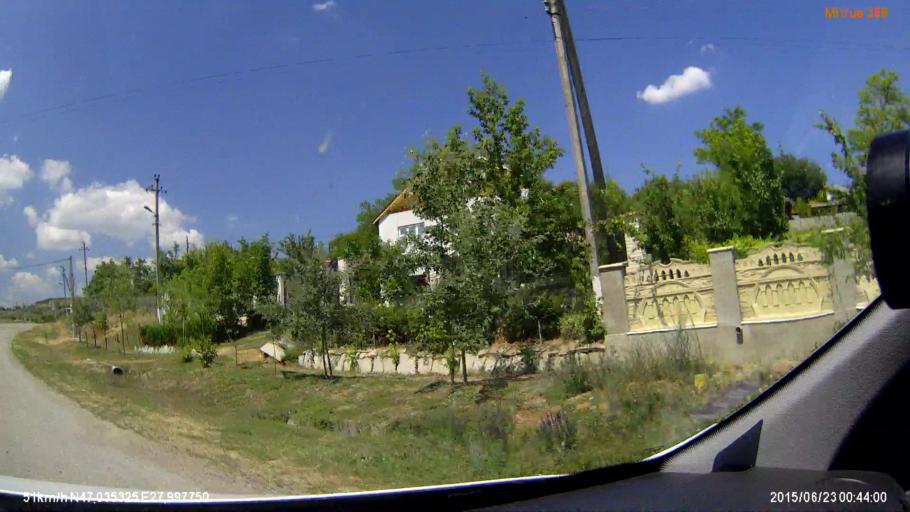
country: RO
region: Iasi
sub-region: Comuna Grozesti
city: Grozesti
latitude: 47.0352
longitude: 27.9979
